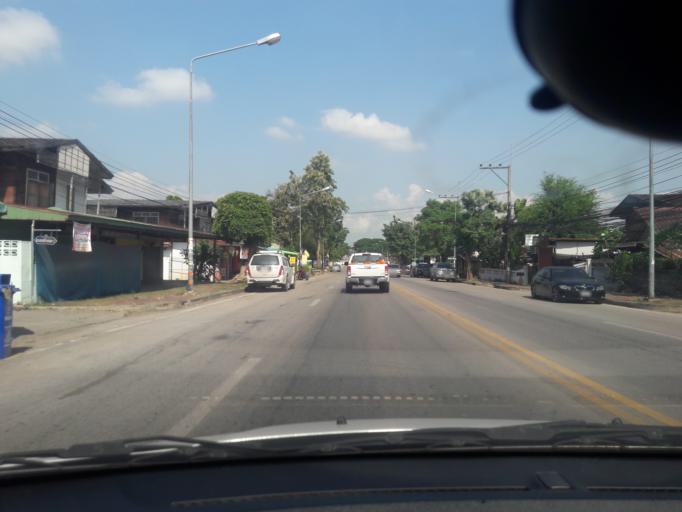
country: TH
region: Lampang
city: Lampang
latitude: 18.2422
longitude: 99.4913
